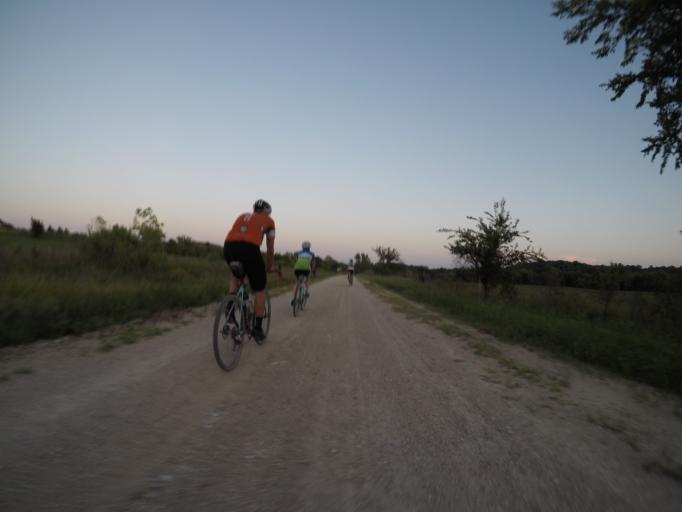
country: US
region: Kansas
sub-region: Riley County
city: Ogden
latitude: 38.9925
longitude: -96.5657
